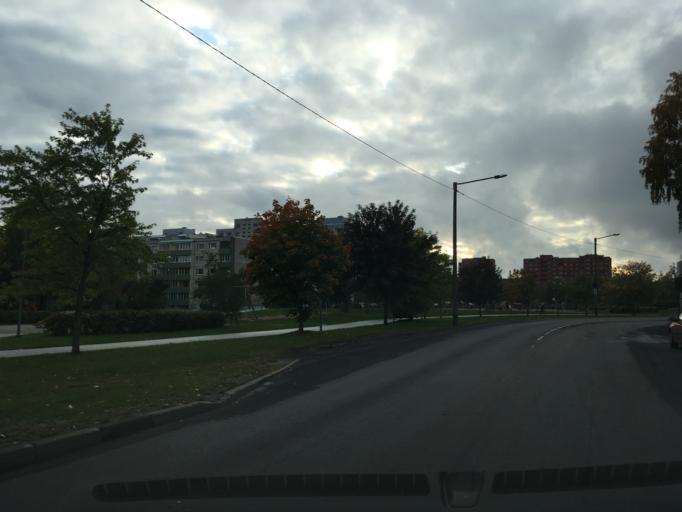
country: EE
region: Harju
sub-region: Tallinna linn
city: Kose
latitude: 59.4431
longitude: 24.8287
